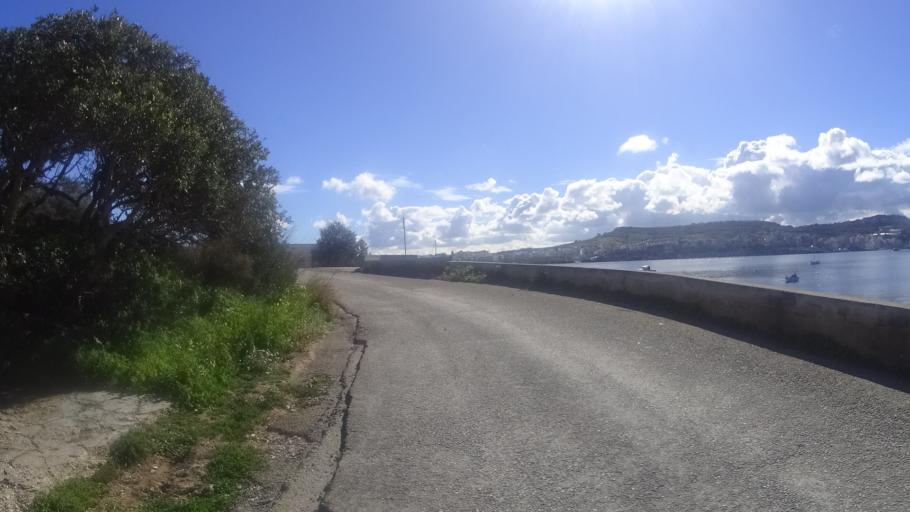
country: MT
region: Saint Paul's Bay
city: San Pawl il-Bahar
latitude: 35.9590
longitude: 14.3925
